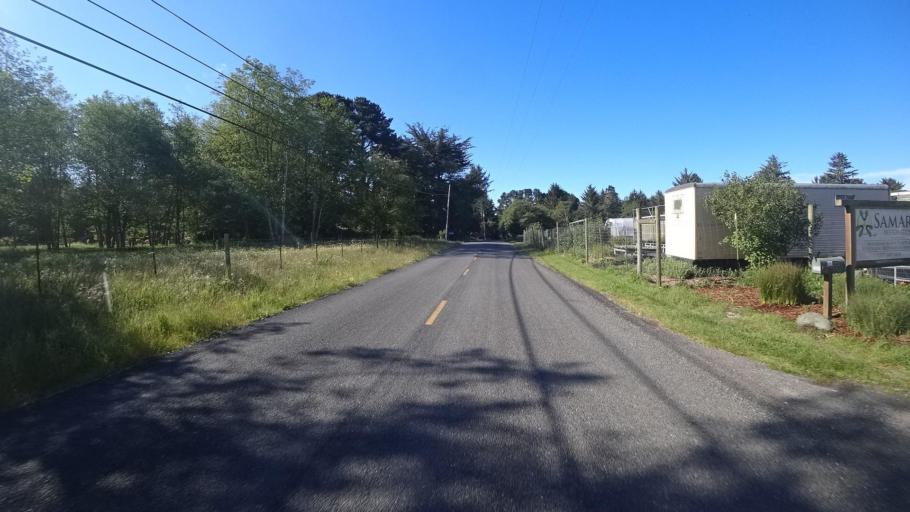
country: US
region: California
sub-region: Humboldt County
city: Westhaven-Moonstone
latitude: 41.0012
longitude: -124.1005
